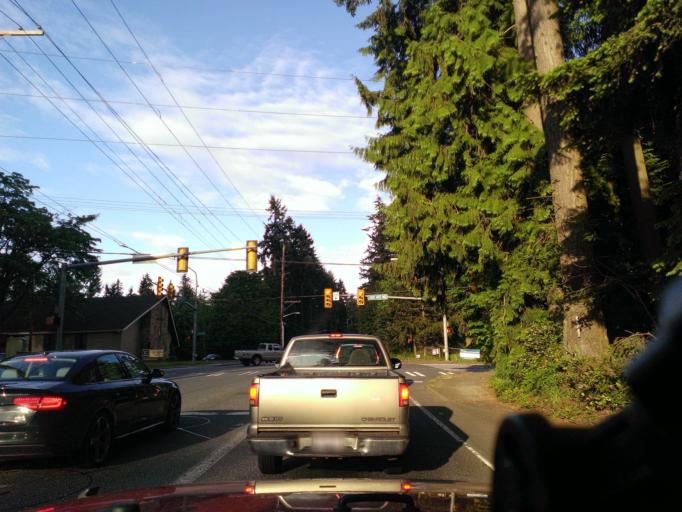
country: US
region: Washington
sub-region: King County
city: Sammamish
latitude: 47.6712
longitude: -122.0632
